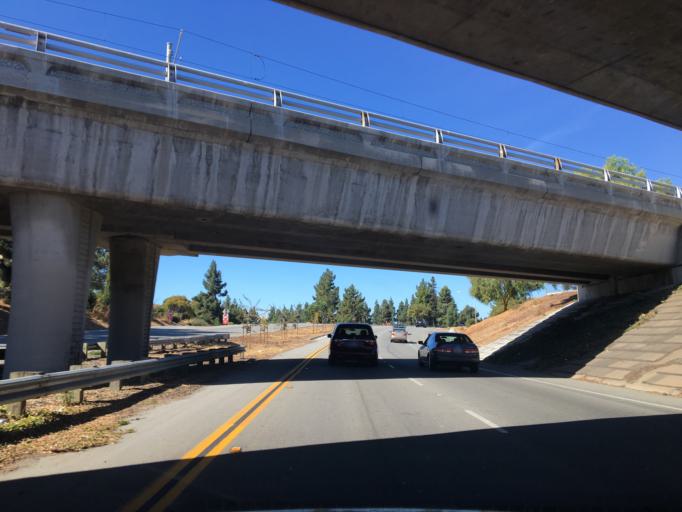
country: US
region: California
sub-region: Santa Clara County
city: Buena Vista
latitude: 37.3131
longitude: -121.9148
